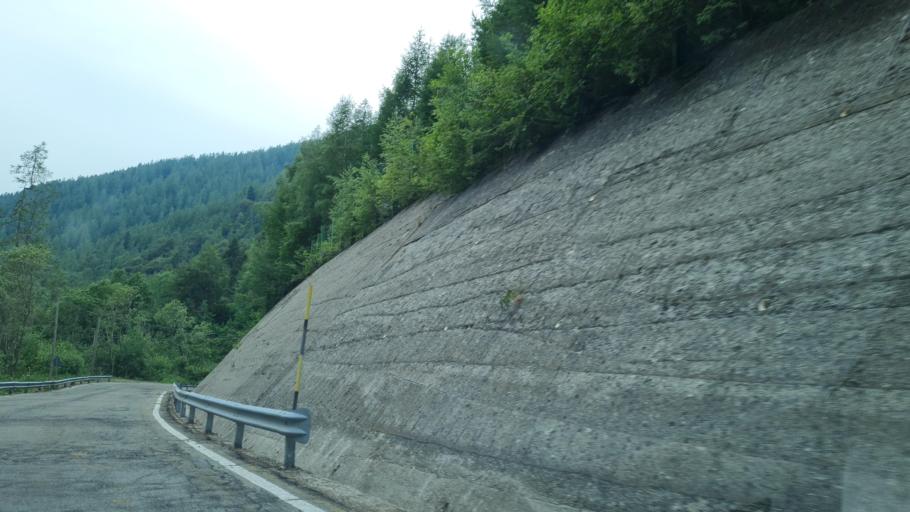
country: IT
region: Piedmont
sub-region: Provincia di Torino
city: Valprato Soana
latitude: 45.5344
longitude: 7.5404
